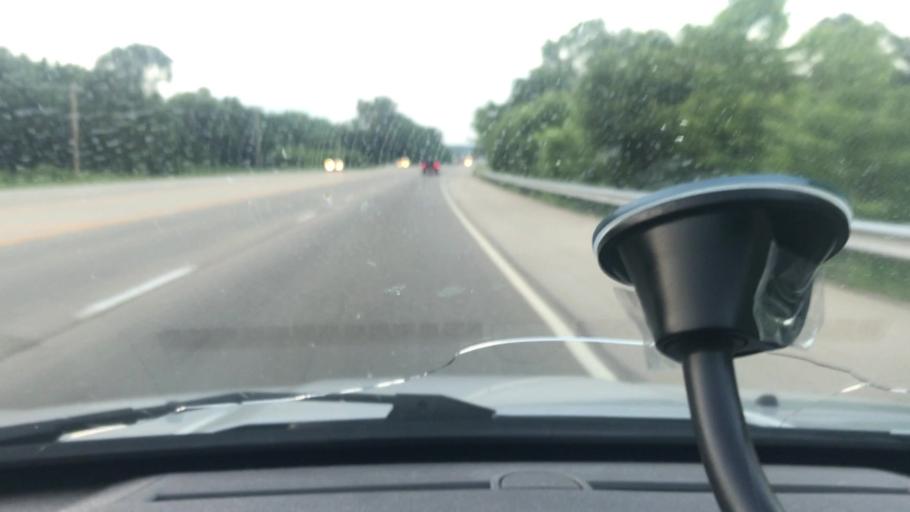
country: US
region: Illinois
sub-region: Tazewell County
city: North Pekin
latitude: 40.6107
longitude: -89.6334
